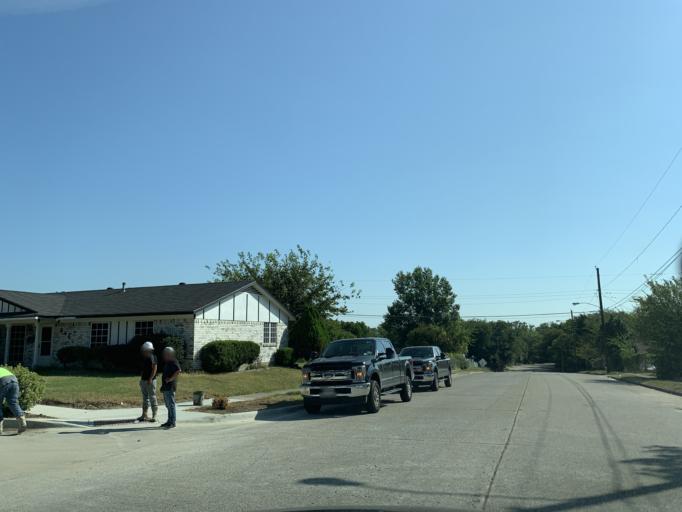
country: US
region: Texas
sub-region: Dallas County
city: Hutchins
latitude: 32.6659
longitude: -96.7524
